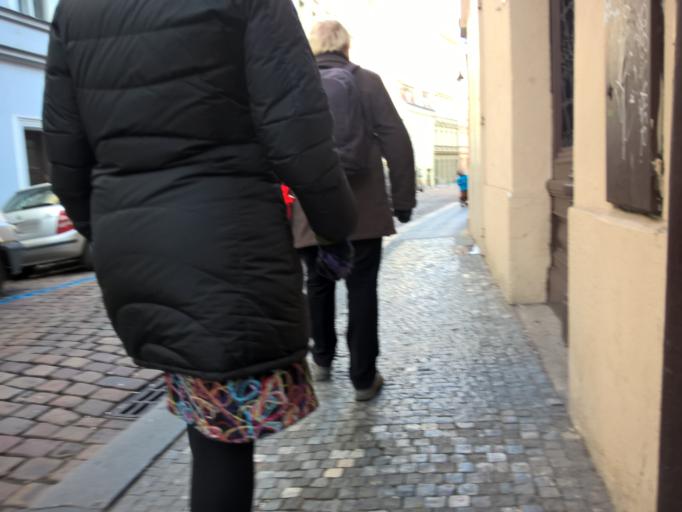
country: CZ
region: Praha
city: Prague
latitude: 50.0899
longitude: 14.4290
